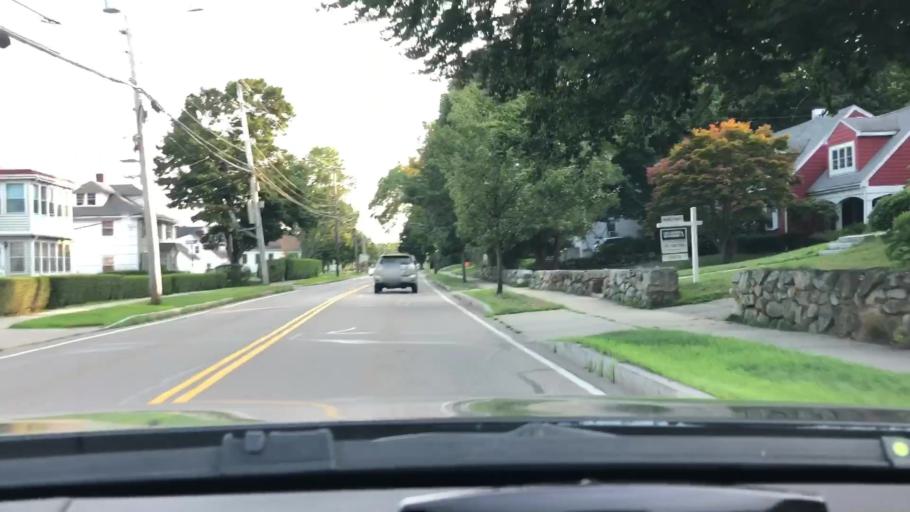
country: US
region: Massachusetts
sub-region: Norfolk County
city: Norwood
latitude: 42.1862
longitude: -71.2109
